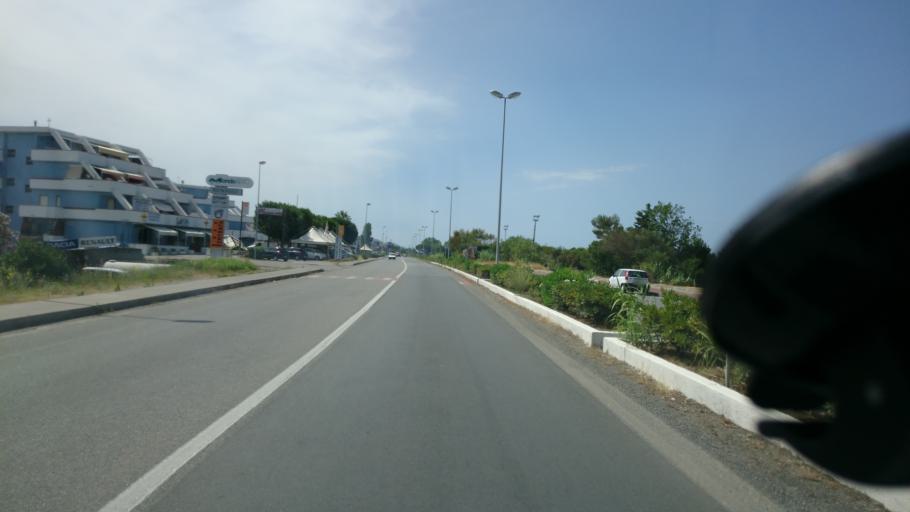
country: IT
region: Calabria
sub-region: Provincia di Cosenza
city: Scalea
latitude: 39.8033
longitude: 15.7908
